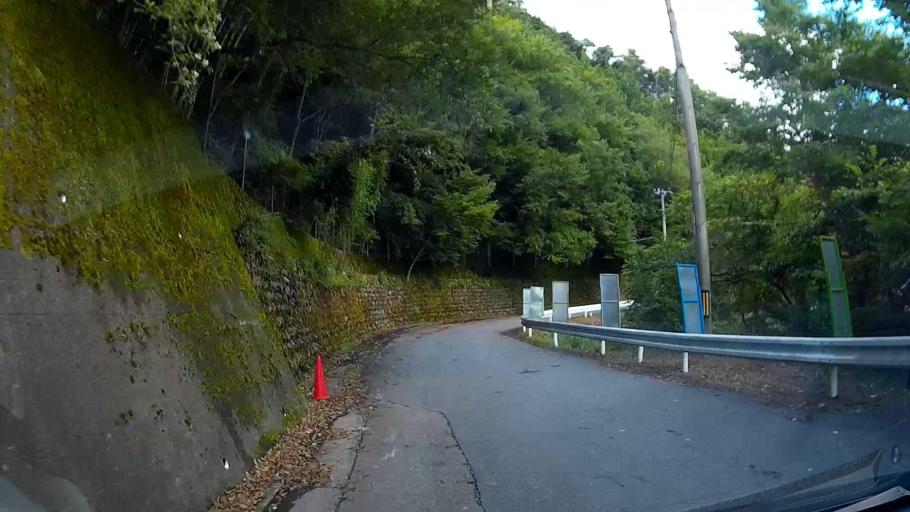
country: JP
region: Shizuoka
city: Shizuoka-shi
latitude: 35.2929
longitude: 138.2192
